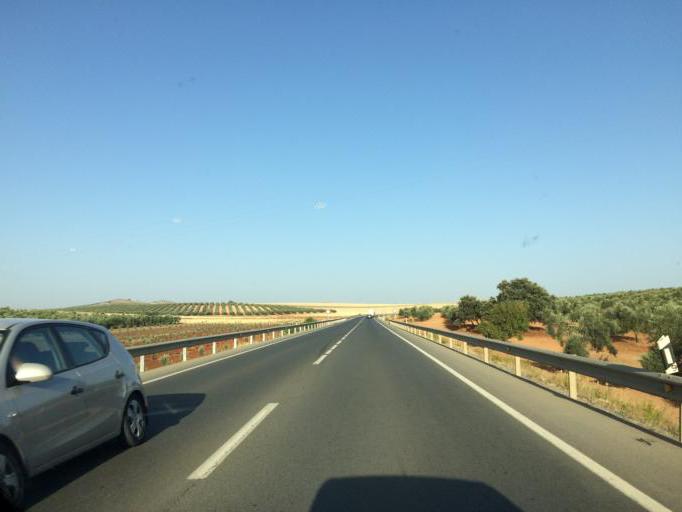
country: ES
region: Andalusia
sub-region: Provincia de Malaga
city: Campillos
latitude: 37.0509
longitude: -4.7957
